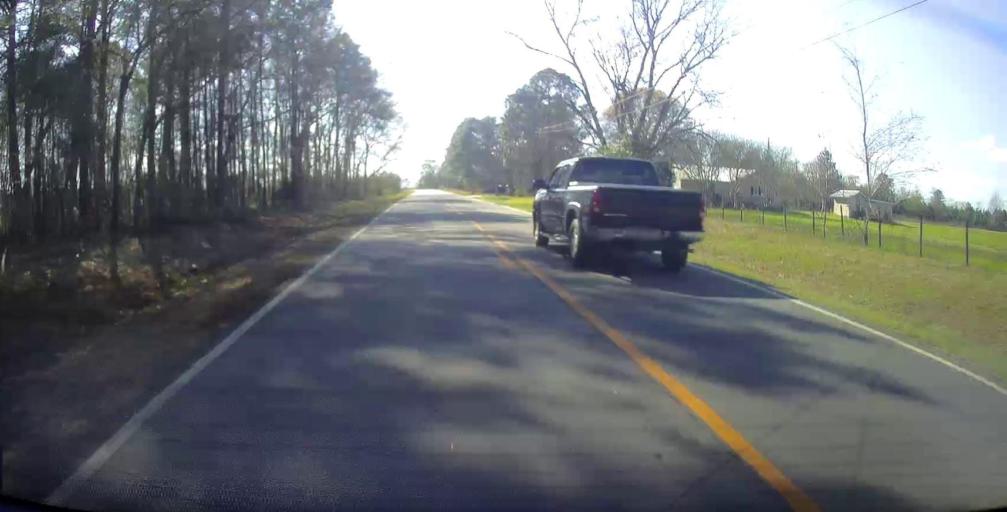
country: US
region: Georgia
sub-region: Laurens County
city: Dublin
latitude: 32.5359
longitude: -82.9650
